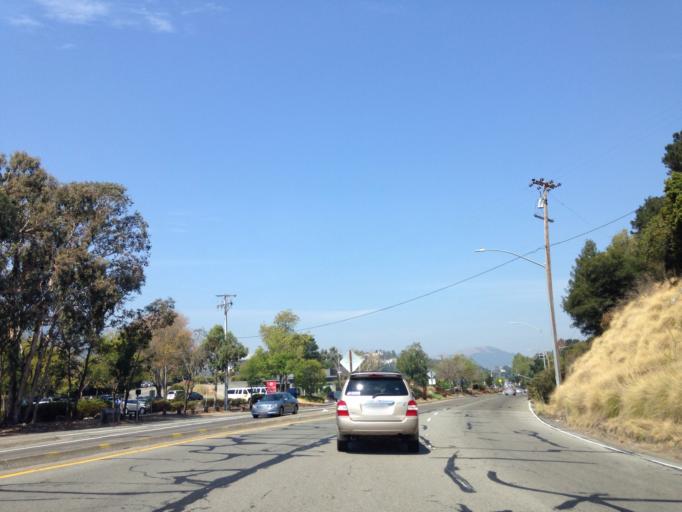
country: US
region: California
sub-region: Marin County
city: Larkspur
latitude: 37.9446
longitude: -122.5174
